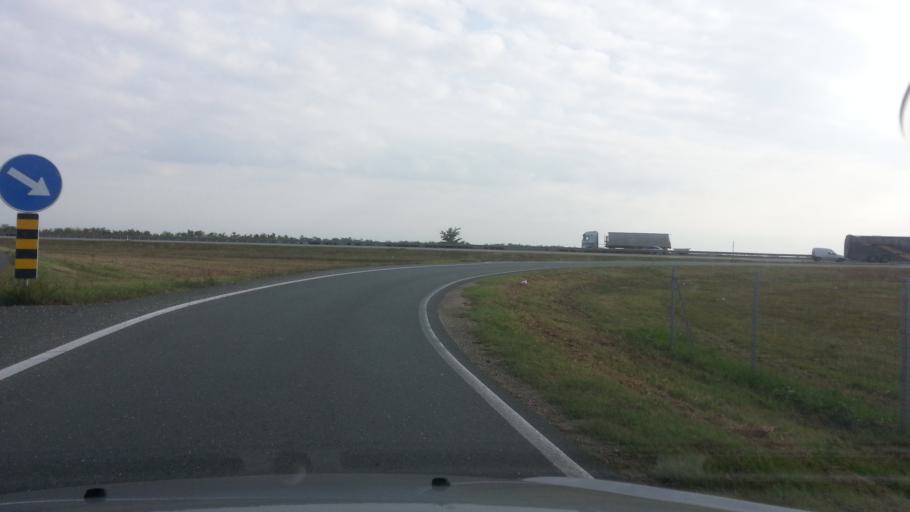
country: RS
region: Autonomna Pokrajina Vojvodina
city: Nova Pazova
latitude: 44.9891
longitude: 20.2112
